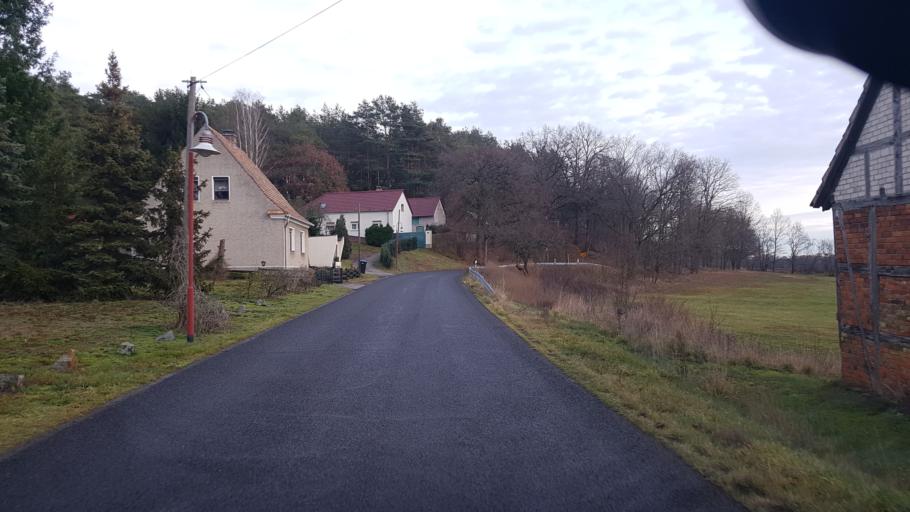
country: DE
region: Brandenburg
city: Hohenbucko
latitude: 51.7425
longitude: 13.4419
